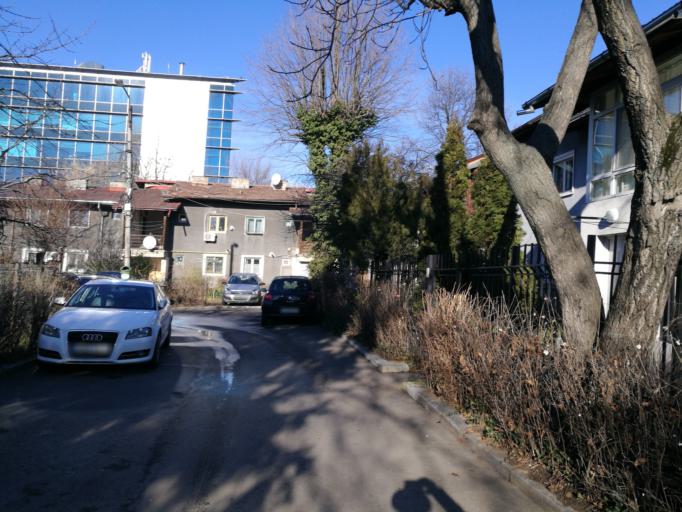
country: RO
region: Ilfov
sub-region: Comuna Otopeni
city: Otopeni
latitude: 44.4941
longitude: 26.0786
